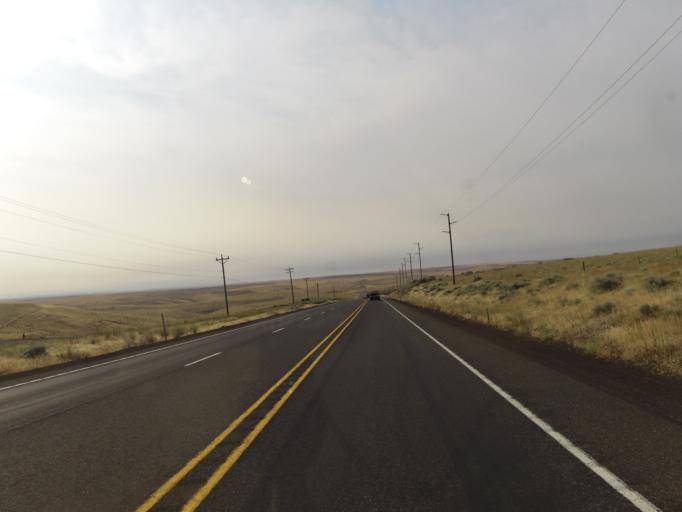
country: US
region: Oregon
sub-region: Sherman County
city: Moro
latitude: 45.5261
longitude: -120.6897
